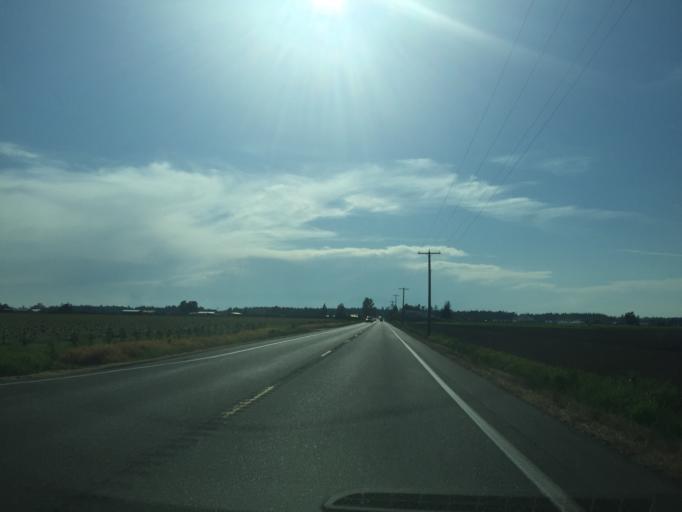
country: US
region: Washington
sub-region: Whatcom County
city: Lynden
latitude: 48.9645
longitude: -122.4748
